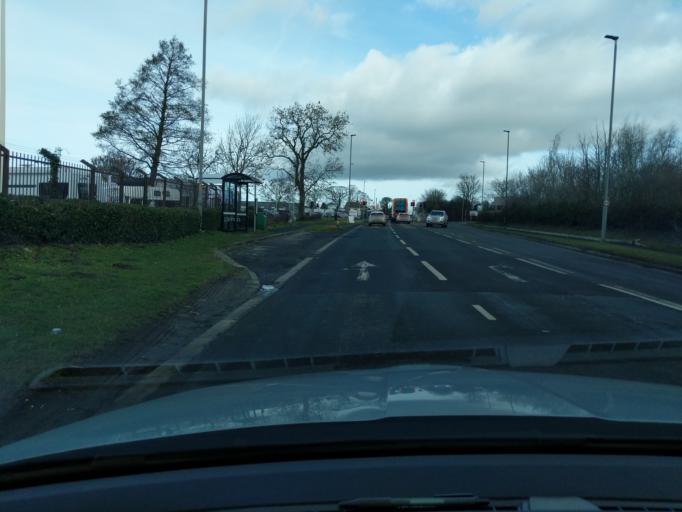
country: GB
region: England
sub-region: North Yorkshire
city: Catterick
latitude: 54.3930
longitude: -1.6536
